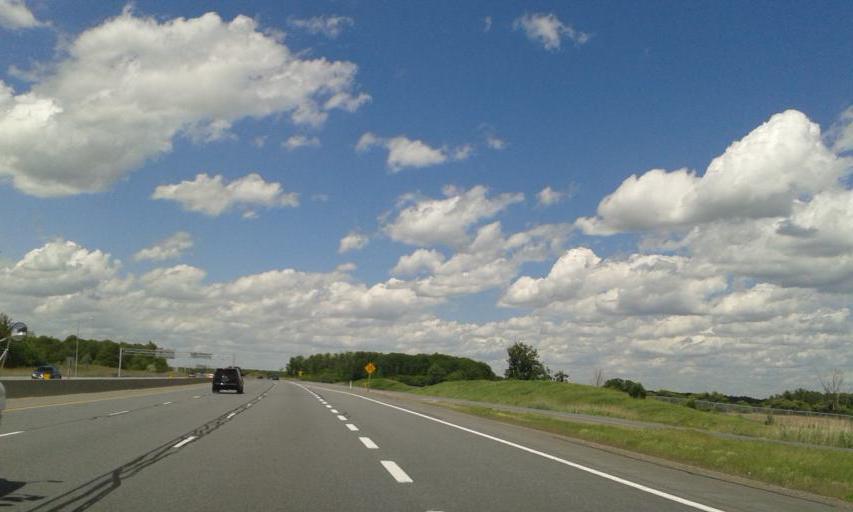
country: CA
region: Ontario
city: Burlington
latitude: 43.4473
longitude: -79.7887
